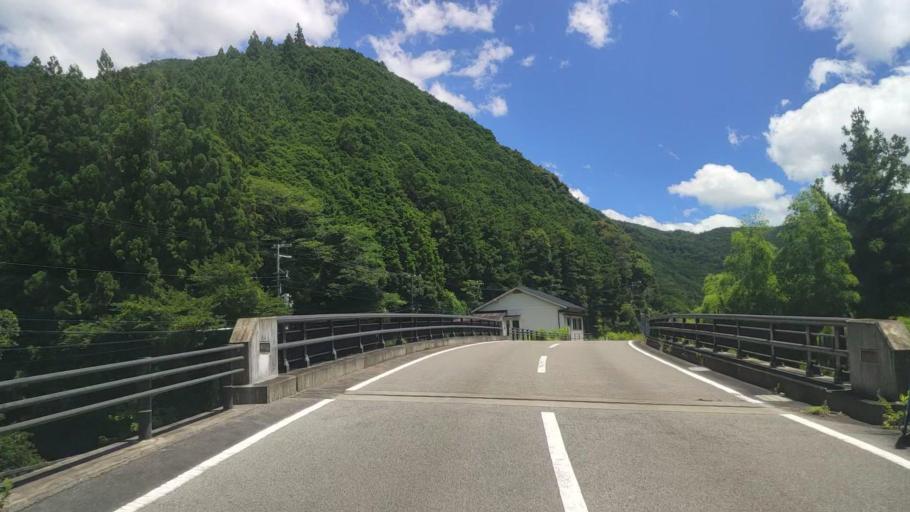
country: JP
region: Wakayama
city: Shingu
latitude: 33.9676
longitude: 135.9769
